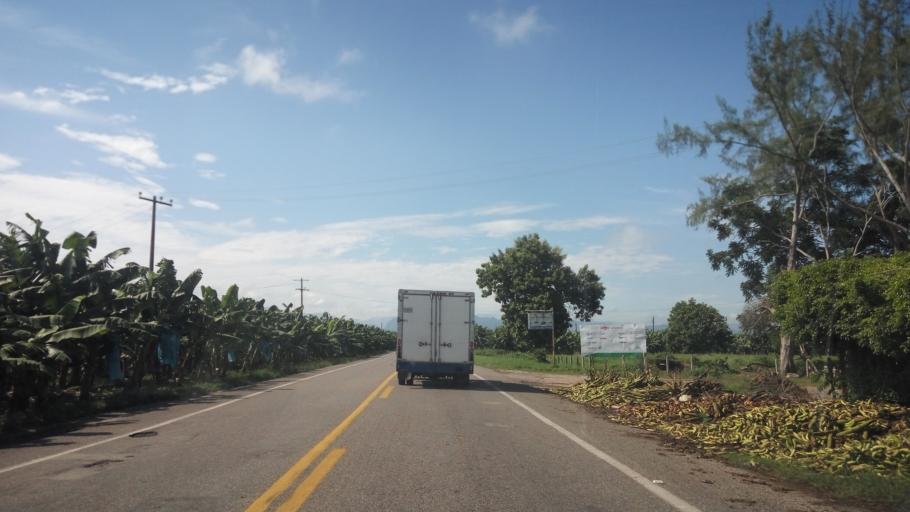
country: MX
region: Tabasco
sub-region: Teapa
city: Eureka y Belen
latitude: 17.6509
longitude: -92.9642
